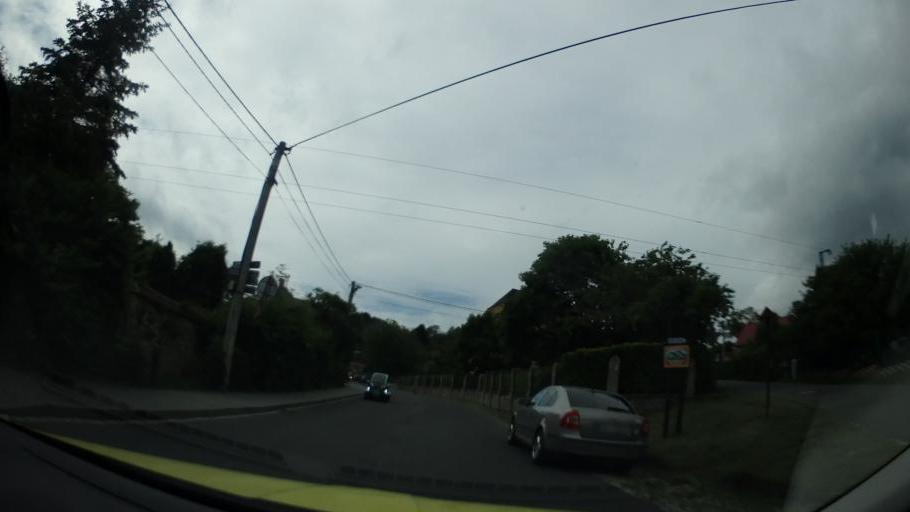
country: CZ
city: Stramberk
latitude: 49.5853
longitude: 18.1302
